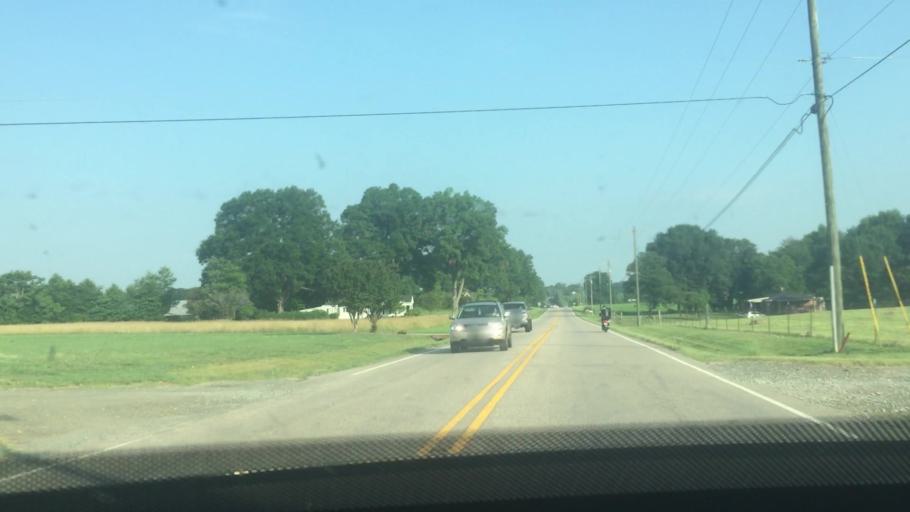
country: US
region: North Carolina
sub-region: Iredell County
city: Mooresville
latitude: 35.5873
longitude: -80.7468
